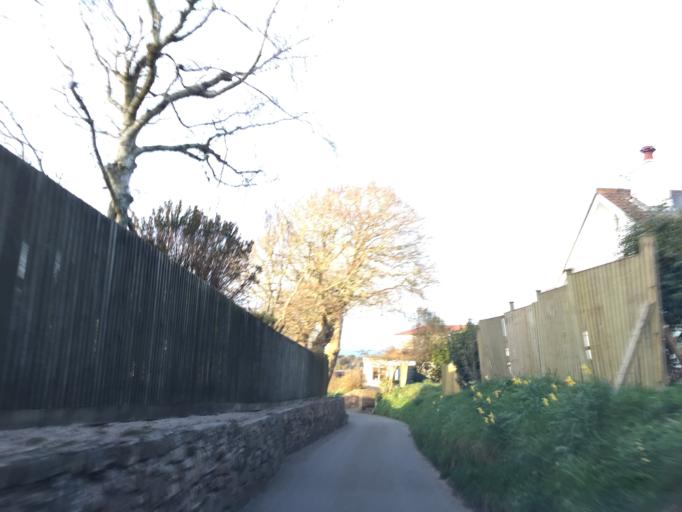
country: JE
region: St Helier
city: Saint Helier
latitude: 49.2291
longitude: -2.0501
